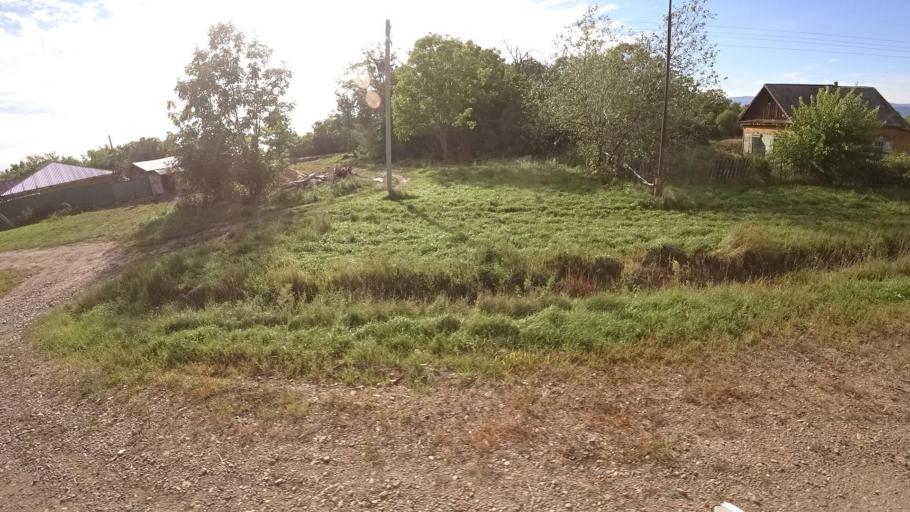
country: RU
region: Primorskiy
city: Dostoyevka
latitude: 44.3015
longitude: 133.4553
